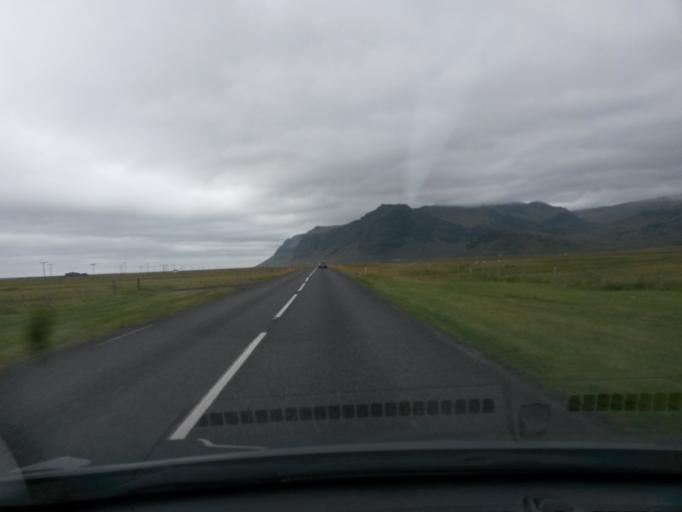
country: IS
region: South
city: Vestmannaeyjar
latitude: 63.5238
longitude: -19.5826
